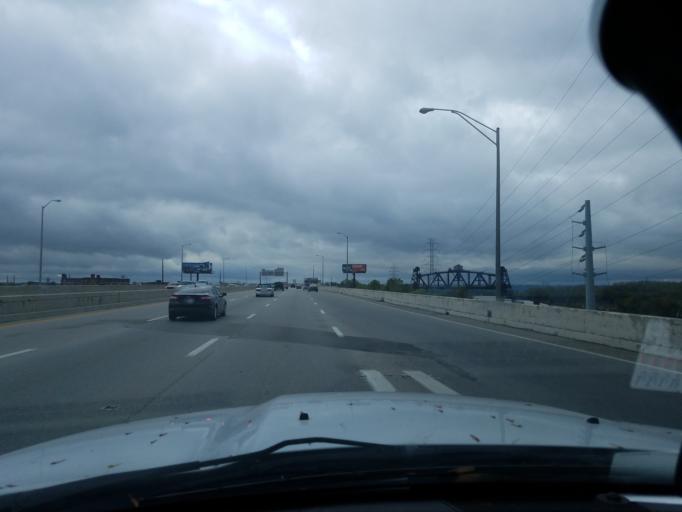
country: US
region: Kentucky
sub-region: Jefferson County
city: Louisville
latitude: 38.2597
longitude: -85.7670
